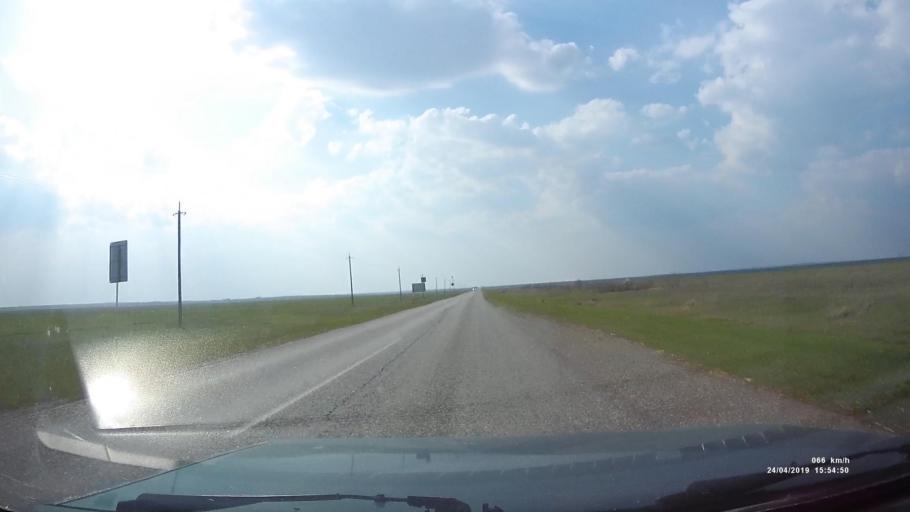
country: RU
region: Kalmykiya
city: Yashalta
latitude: 46.5867
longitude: 42.5600
